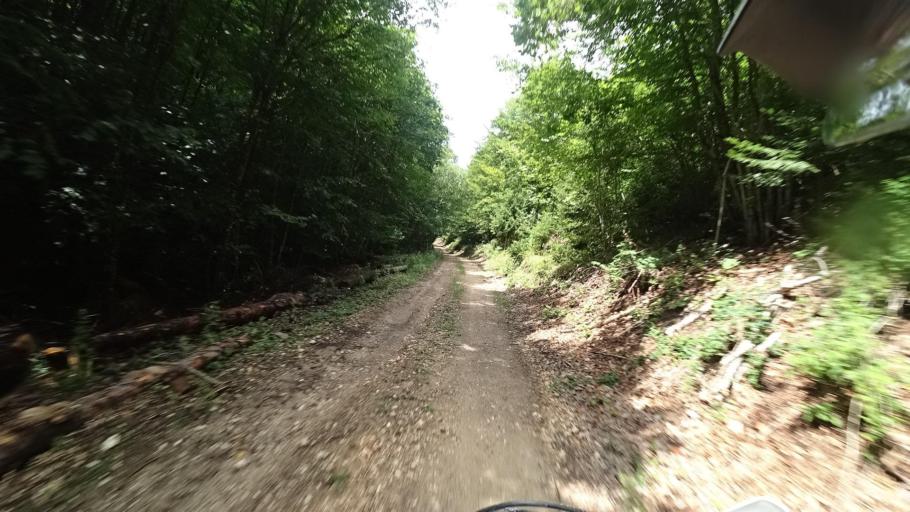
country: HR
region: Licko-Senjska
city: Otocac
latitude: 44.8744
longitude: 15.4206
